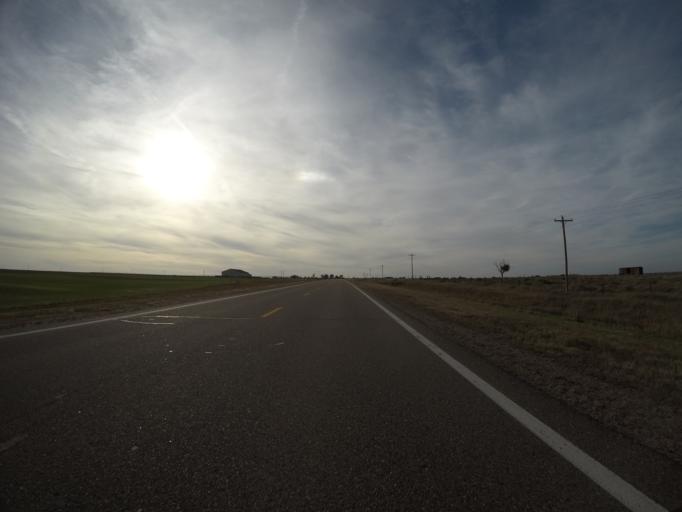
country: US
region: Kansas
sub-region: Cheyenne County
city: Saint Francis
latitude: 39.7566
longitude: -101.7637
